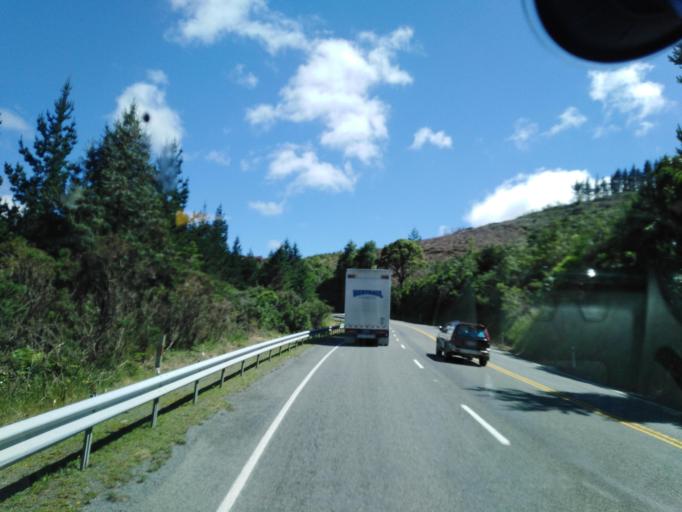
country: NZ
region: Nelson
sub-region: Nelson City
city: Nelson
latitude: -41.1933
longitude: 173.5574
